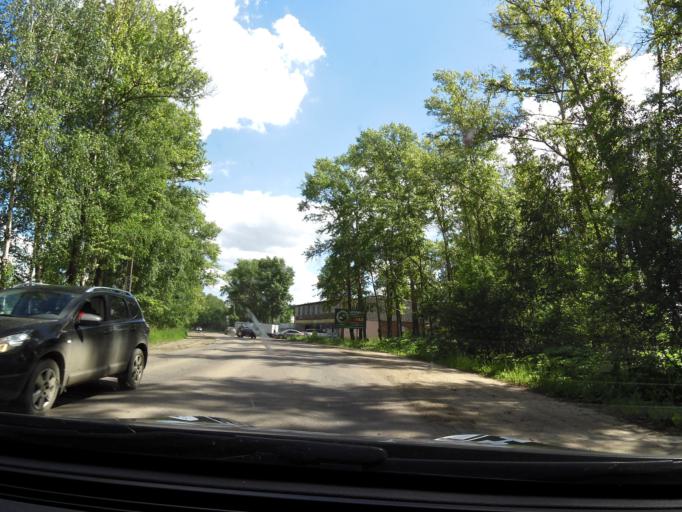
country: RU
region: Vologda
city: Vologda
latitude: 59.2380
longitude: 39.8135
